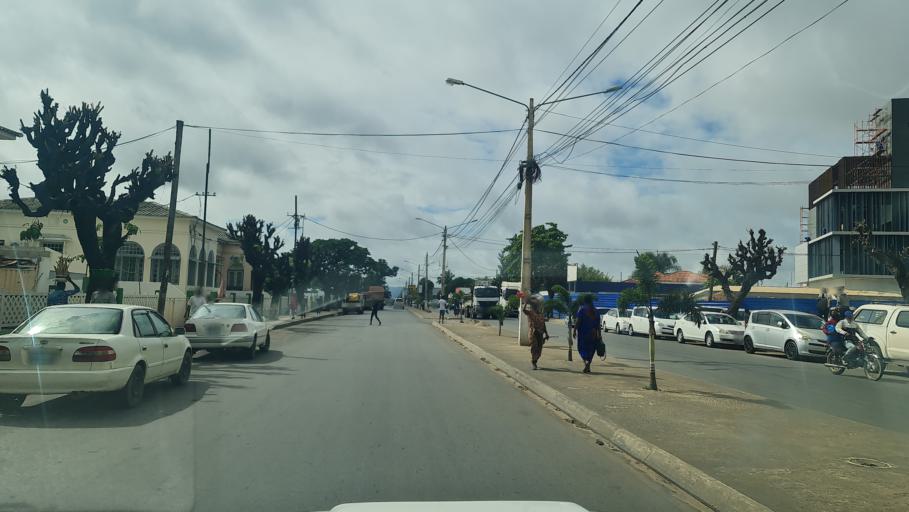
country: MZ
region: Nampula
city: Nampula
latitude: -15.1137
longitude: 39.2632
